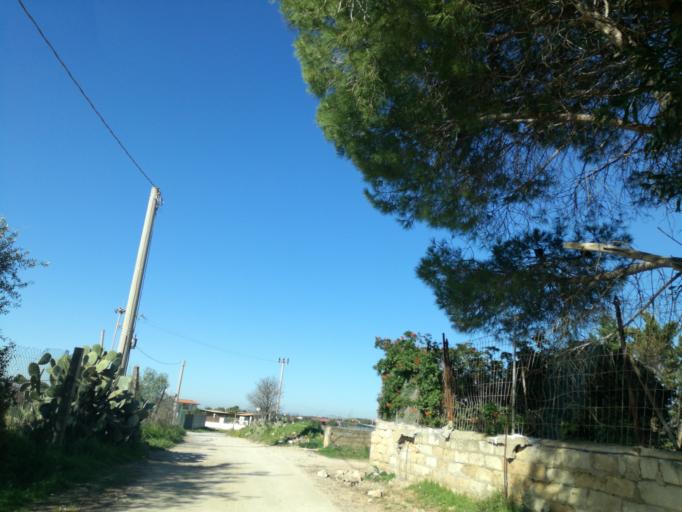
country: IT
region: Sicily
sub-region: Provincia di Caltanissetta
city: Niscemi
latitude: 37.0583
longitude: 14.3584
